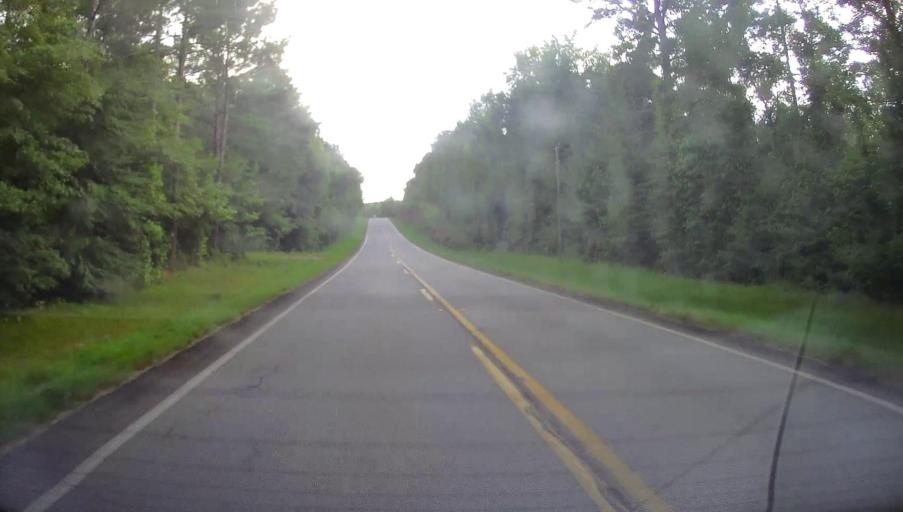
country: US
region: Georgia
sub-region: Crawford County
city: Knoxville
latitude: 32.8439
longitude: -84.0107
